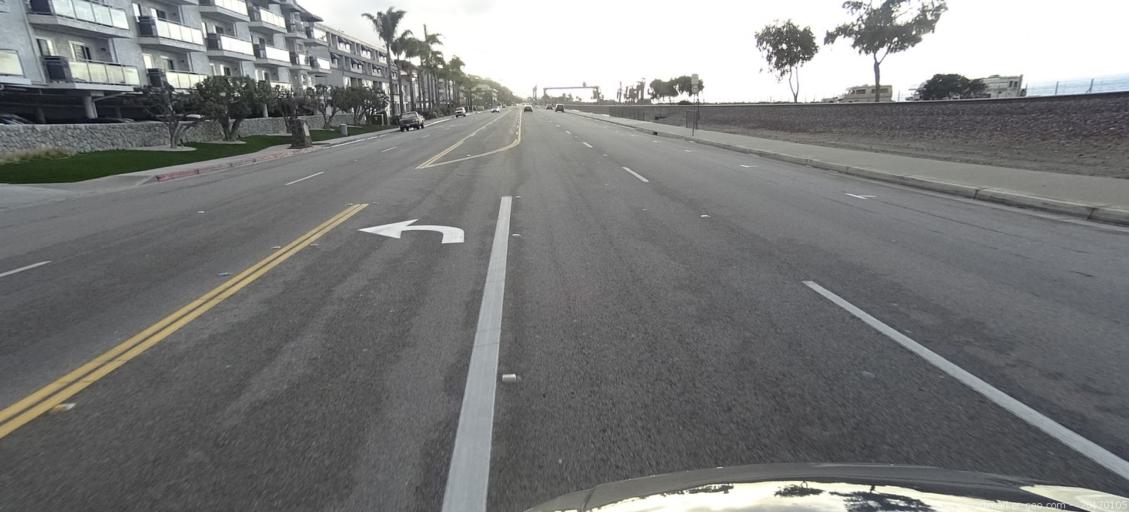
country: US
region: California
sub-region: Orange County
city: Dana Point
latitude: 33.4607
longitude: -117.6762
